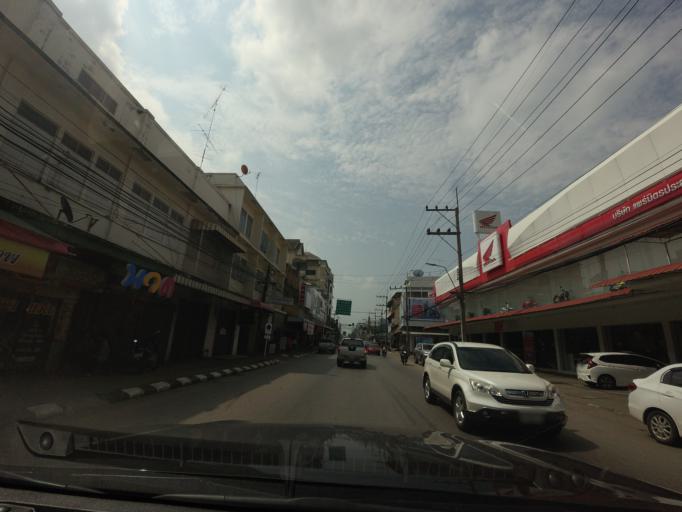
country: TH
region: Phrae
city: Phrae
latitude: 18.1389
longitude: 100.1480
